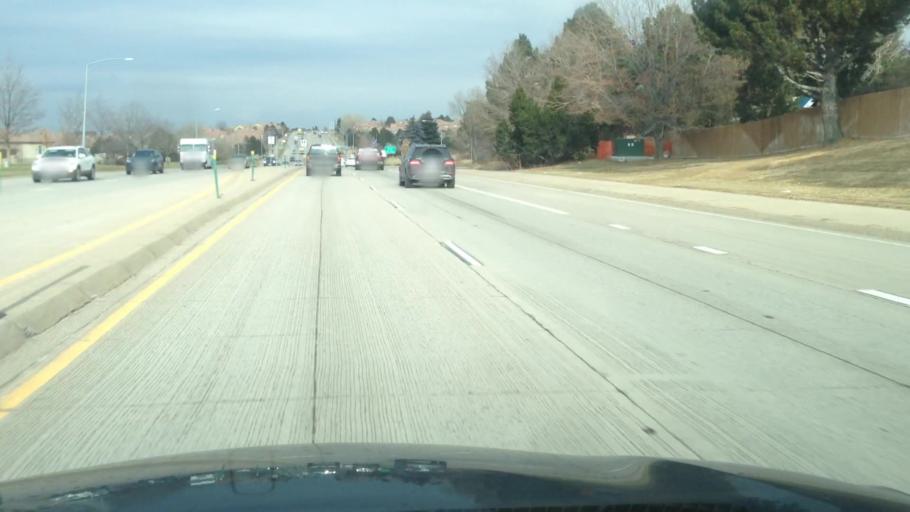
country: US
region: Colorado
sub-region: Arapahoe County
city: Dove Valley
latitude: 39.6280
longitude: -104.8239
